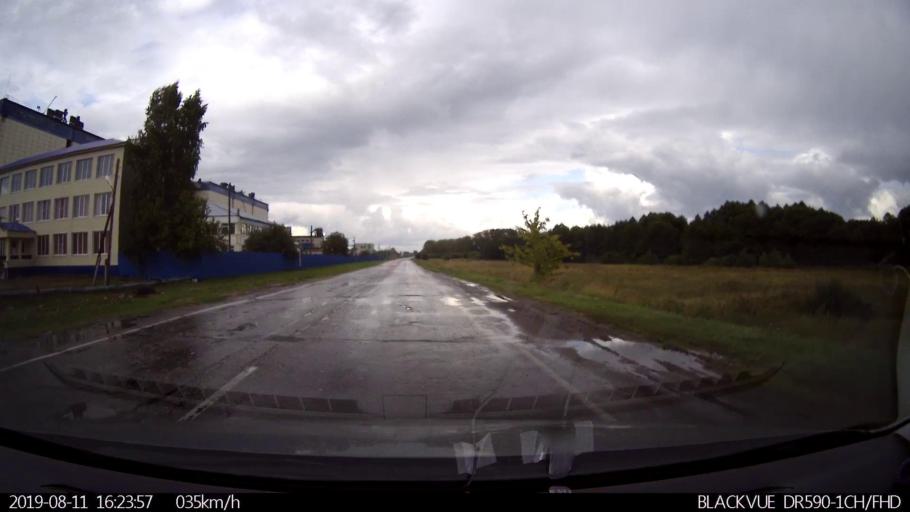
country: RU
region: Ulyanovsk
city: Mayna
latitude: 54.0978
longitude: 47.5902
